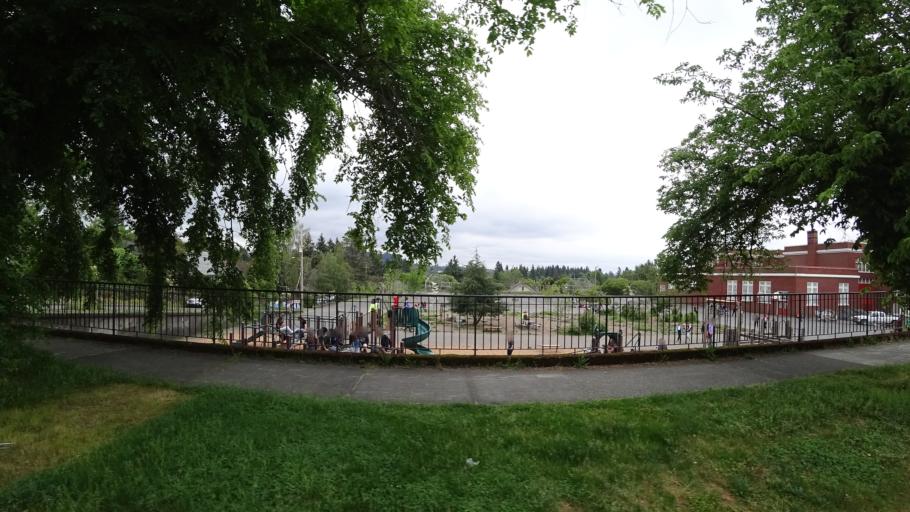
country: US
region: Oregon
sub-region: Multnomah County
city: Lents
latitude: 45.5399
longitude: -122.6030
